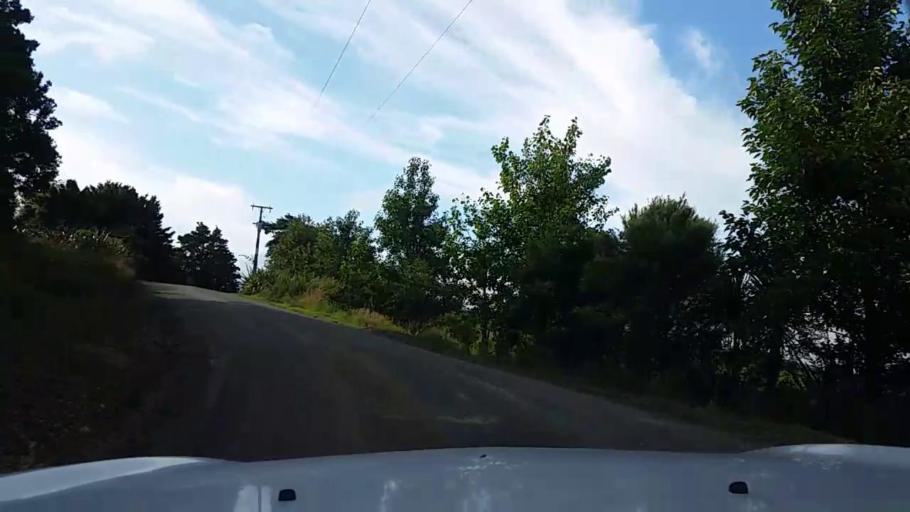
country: NZ
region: Northland
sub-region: Whangarei
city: Maungatapere
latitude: -35.6749
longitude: 174.1762
